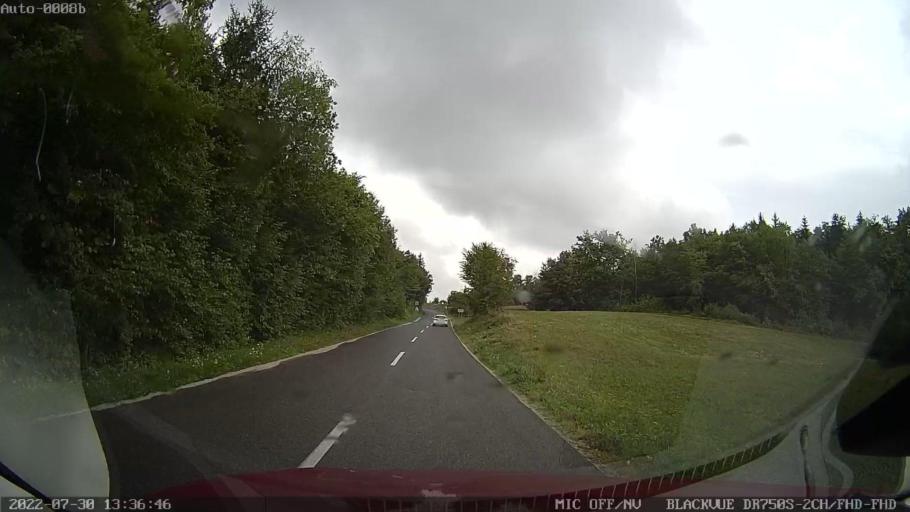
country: SI
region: Zuzemberk
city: Zuzemberk
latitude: 45.8724
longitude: 14.9220
